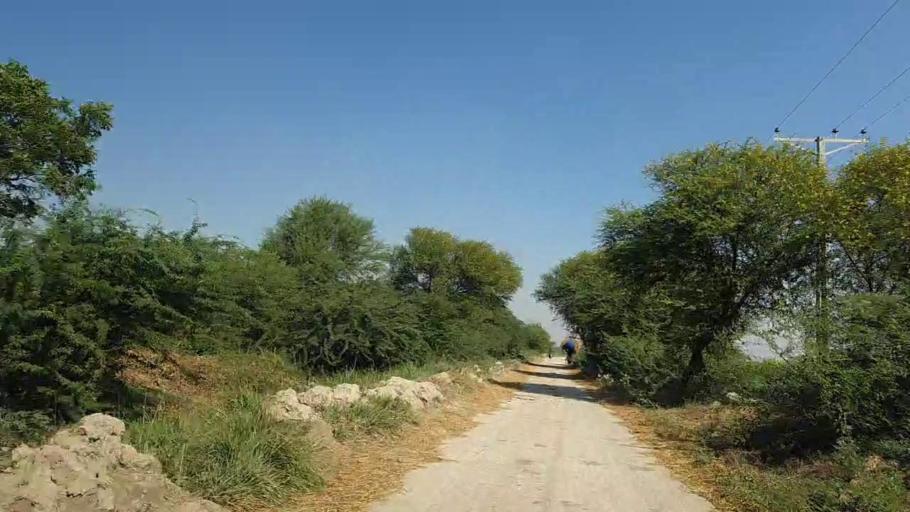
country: PK
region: Sindh
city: Daro Mehar
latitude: 24.7817
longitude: 68.1608
